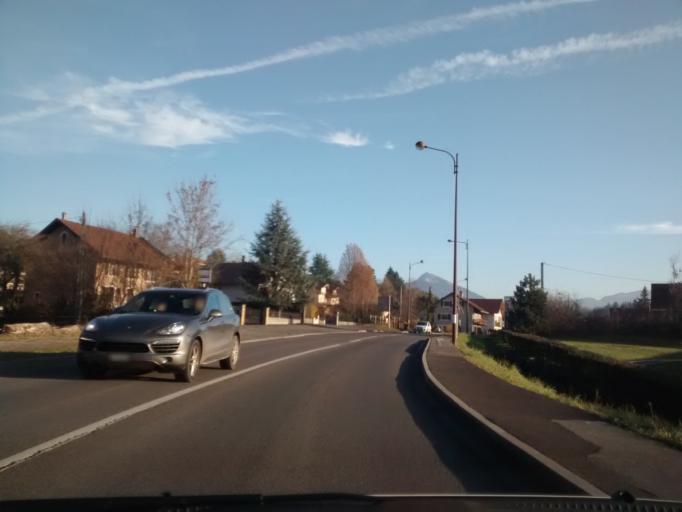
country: FR
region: Rhone-Alpes
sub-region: Departement de la Haute-Savoie
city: Bonne-sur-Menoge
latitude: 46.1707
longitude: 6.3160
